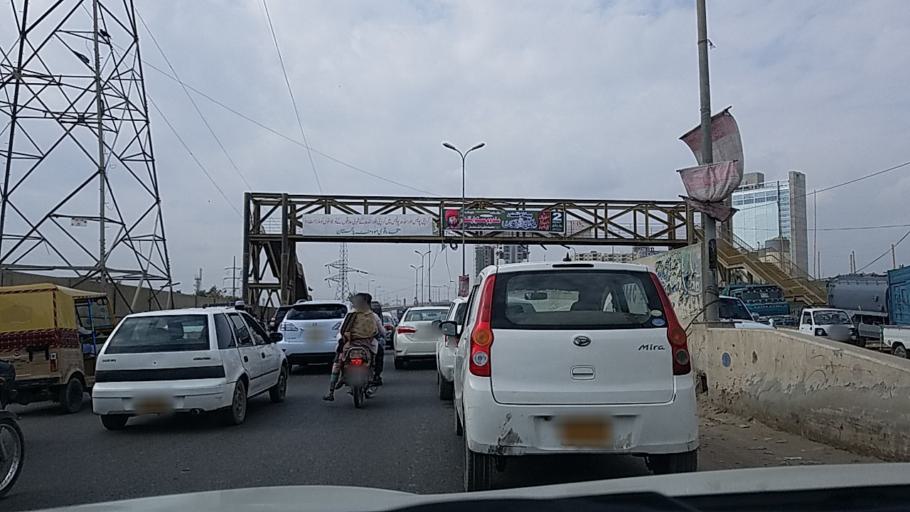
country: PK
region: Sindh
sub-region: Karachi District
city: Karachi
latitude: 24.8280
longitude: 67.0839
